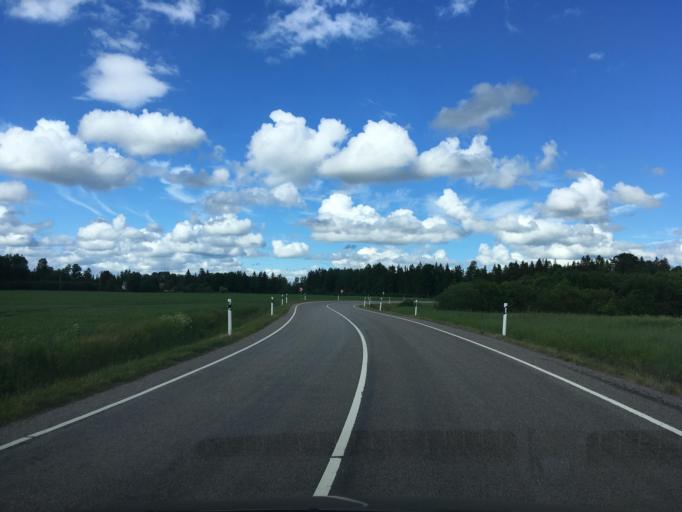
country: EE
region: Paernumaa
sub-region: Tootsi vald
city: Tootsi
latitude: 58.6578
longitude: 24.7173
